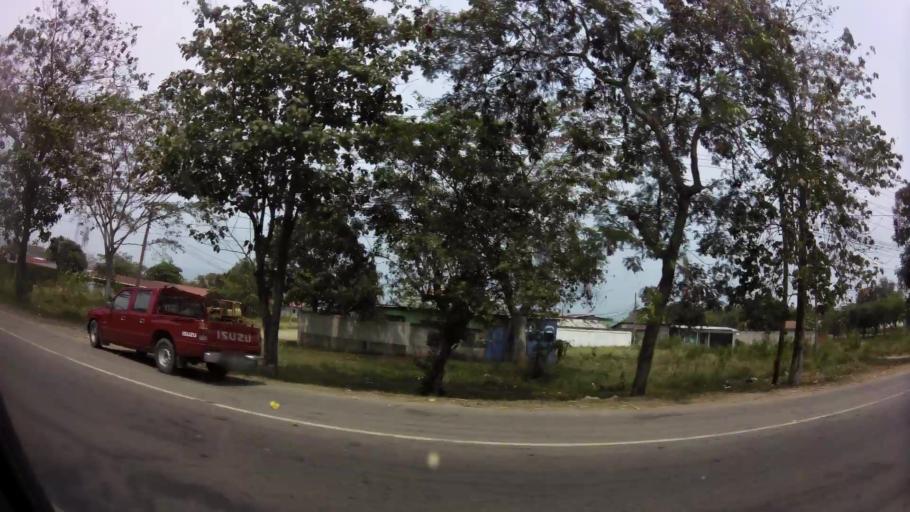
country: HN
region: Cortes
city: Villanueva
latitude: 15.3319
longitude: -87.9918
